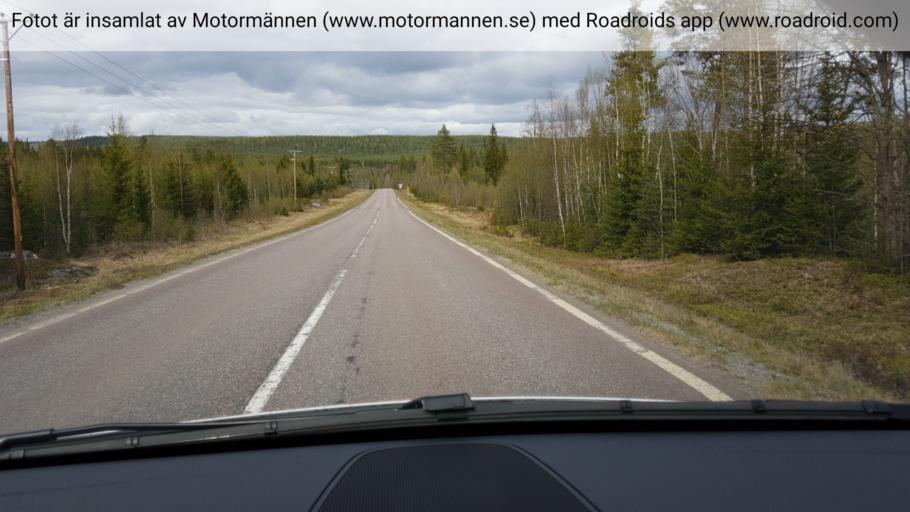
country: SE
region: Jaemtland
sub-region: Ragunda Kommun
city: Hammarstrand
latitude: 63.2058
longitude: 15.9472
